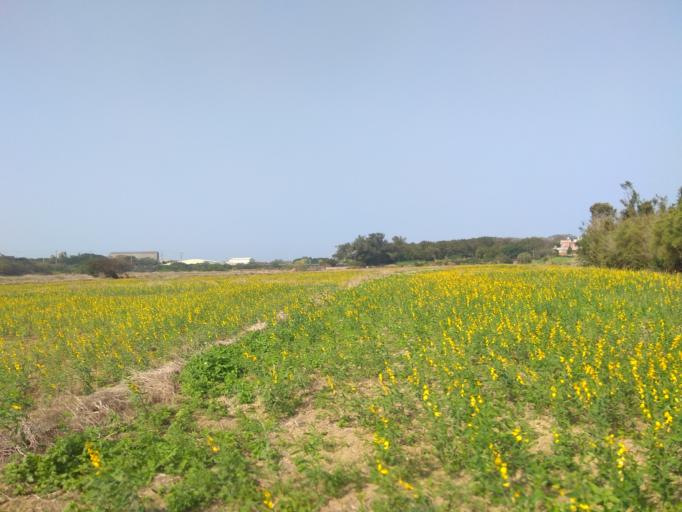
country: TW
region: Taiwan
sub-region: Hsinchu
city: Zhubei
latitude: 24.9949
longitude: 121.0390
